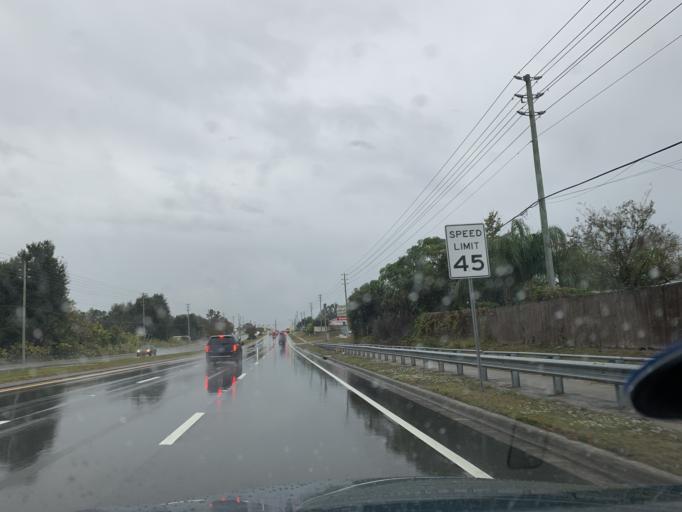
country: US
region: Florida
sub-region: Pasco County
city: Bayonet Point
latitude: 28.3228
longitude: -82.6662
